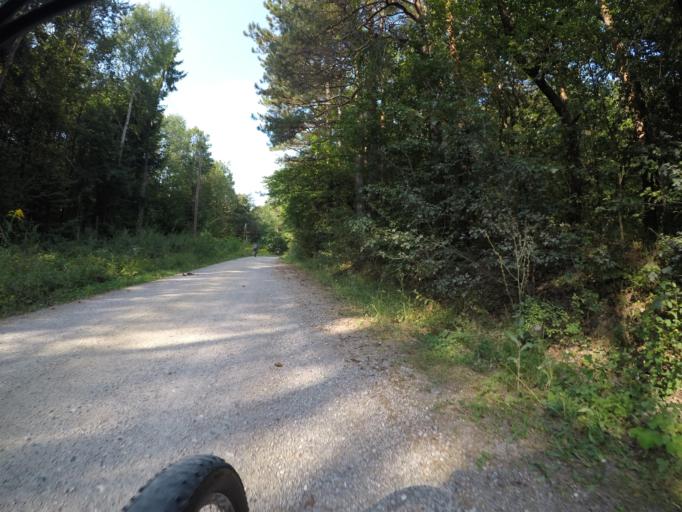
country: AT
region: Lower Austria
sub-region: Politischer Bezirk Baden
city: Berndorf
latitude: 47.9637
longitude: 16.1371
